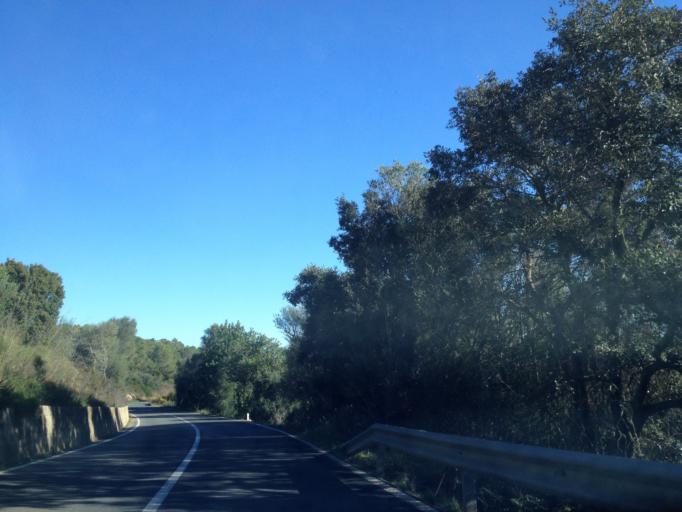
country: ES
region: Balearic Islands
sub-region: Illes Balears
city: Sineu
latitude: 39.6533
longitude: 3.0311
